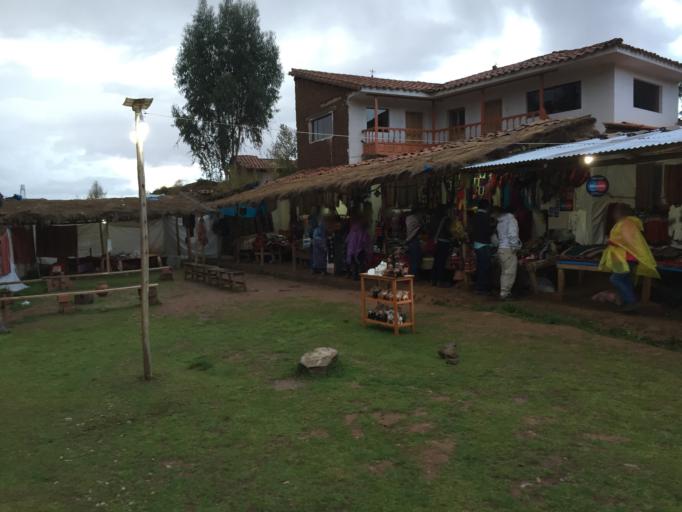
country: PE
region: Cusco
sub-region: Provincia de Urubamba
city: Chinchero
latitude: -13.3898
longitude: -72.0514
